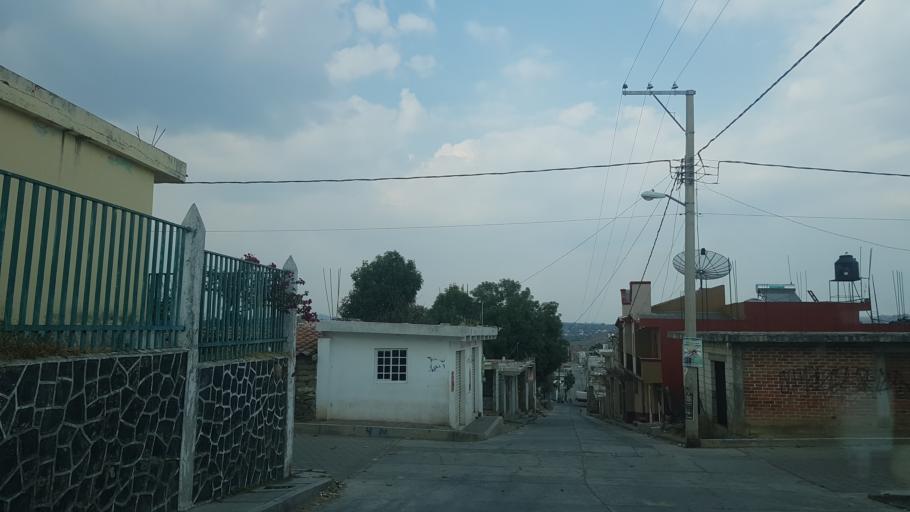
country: MX
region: Puebla
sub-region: Santa Isabel Cholula
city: San Martin Tlamapa
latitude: 18.9790
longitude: -98.3977
